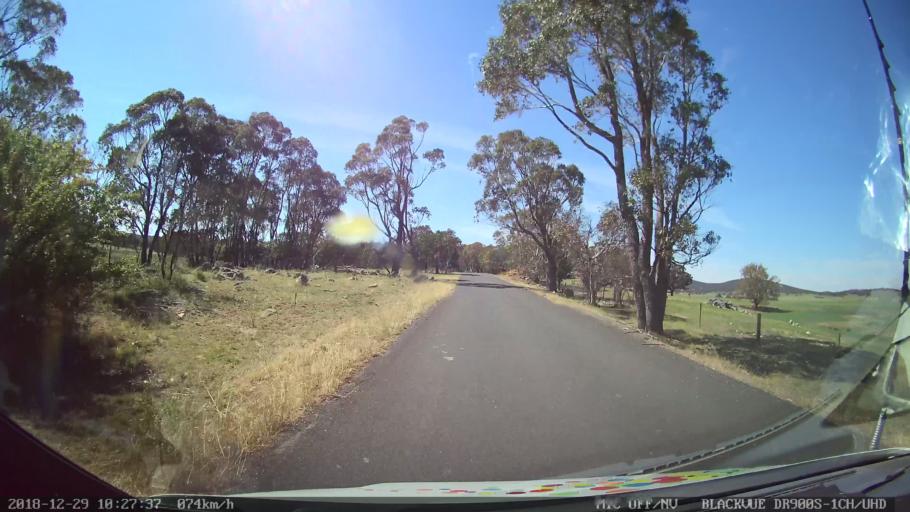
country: AU
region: New South Wales
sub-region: Yass Valley
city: Gundaroo
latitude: -34.9359
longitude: 149.4511
